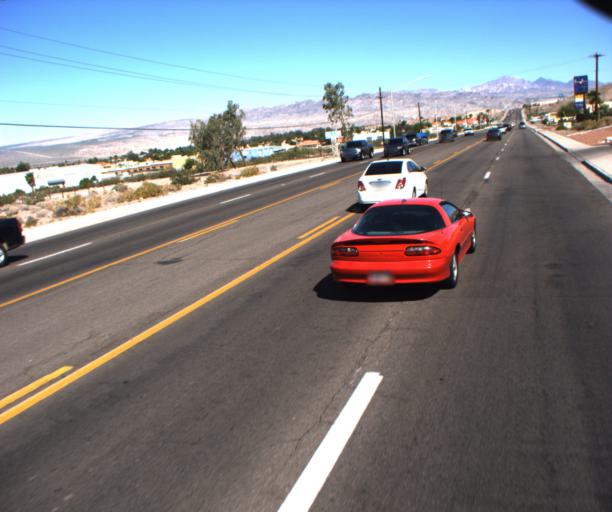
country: US
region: Arizona
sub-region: Mohave County
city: Bullhead City
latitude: 35.0713
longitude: -114.5900
